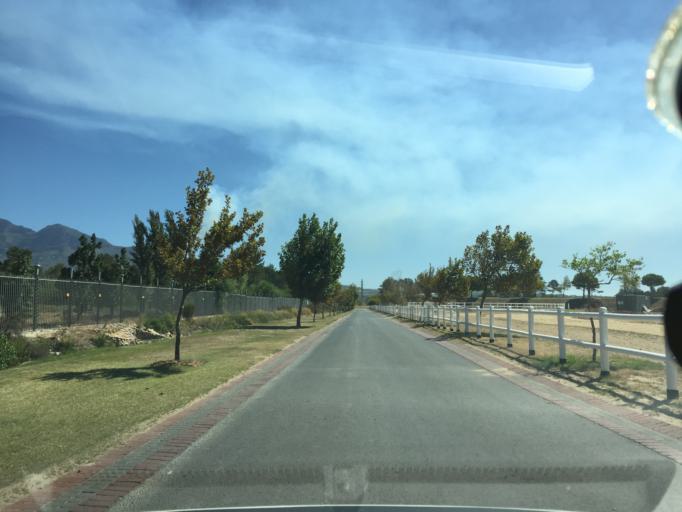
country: ZA
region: Western Cape
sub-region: Cape Winelands District Municipality
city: Paarl
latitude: -33.8053
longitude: 18.9723
